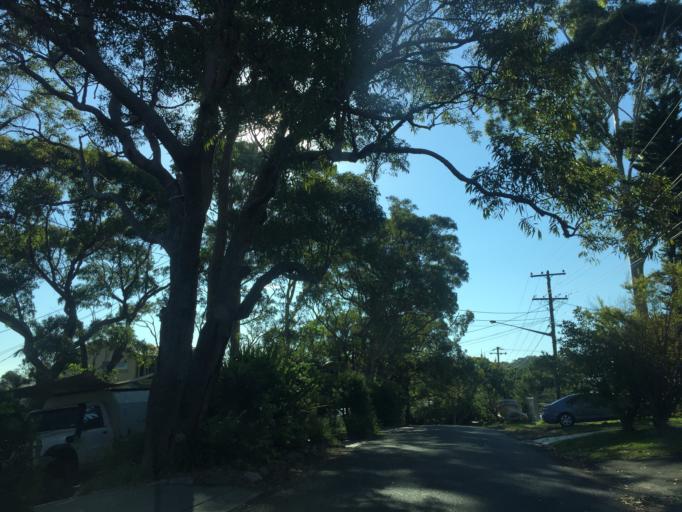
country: AU
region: New South Wales
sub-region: Pittwater
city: North Narrabeen
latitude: -33.7045
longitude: 151.2814
